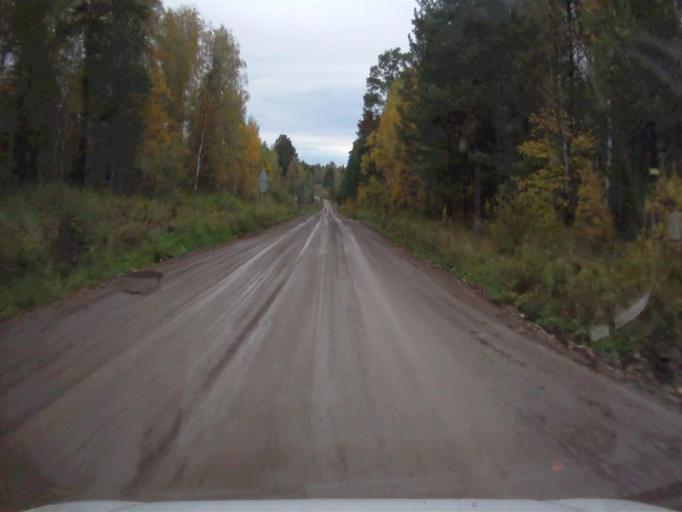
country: RU
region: Chelyabinsk
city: Nyazepetrovsk
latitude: 56.0867
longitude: 59.4181
